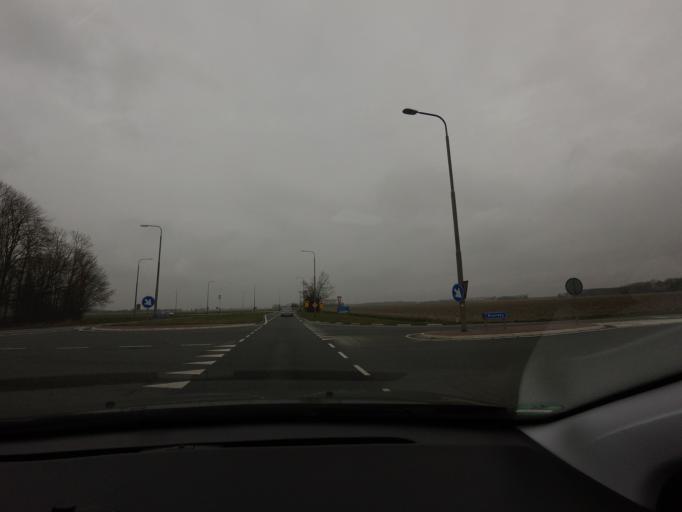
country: NL
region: Flevoland
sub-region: Gemeente Dronten
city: Dronten
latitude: 52.5748
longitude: 5.6440
